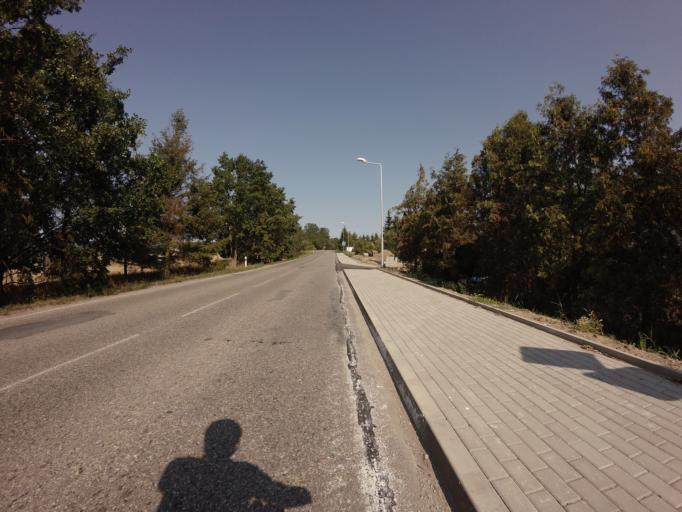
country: CZ
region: Central Bohemia
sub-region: Okres Benesov
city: Benesov
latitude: 49.8014
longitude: 14.6536
